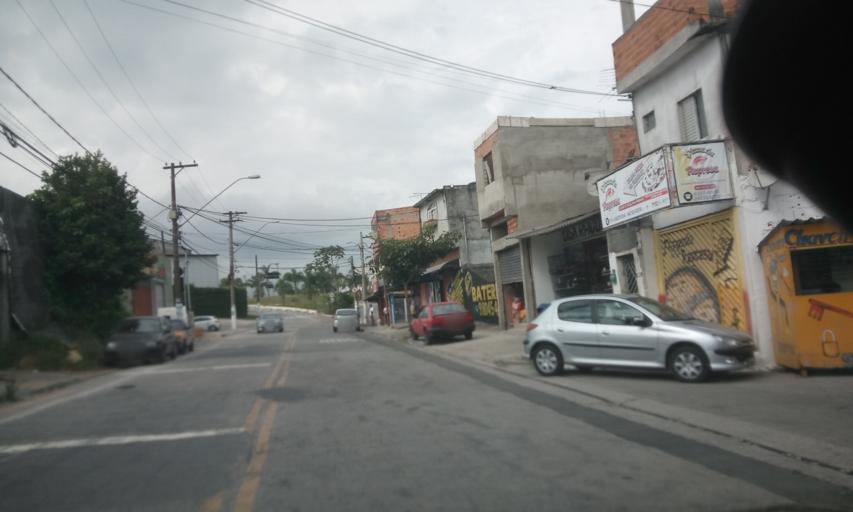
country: BR
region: Sao Paulo
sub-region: Sao Bernardo Do Campo
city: Sao Bernardo do Campo
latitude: -23.7717
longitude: -46.5994
